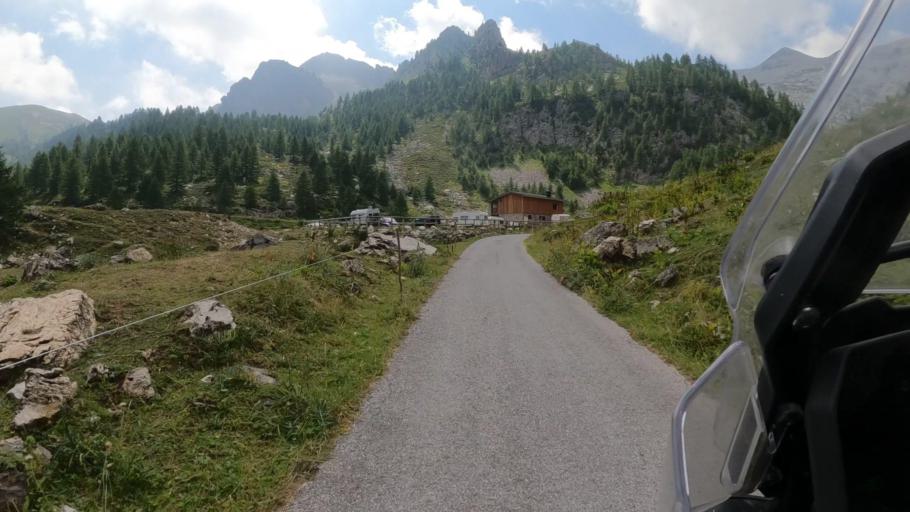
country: IT
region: Piedmont
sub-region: Provincia di Cuneo
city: Marmora
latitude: 44.3989
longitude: 7.1068
